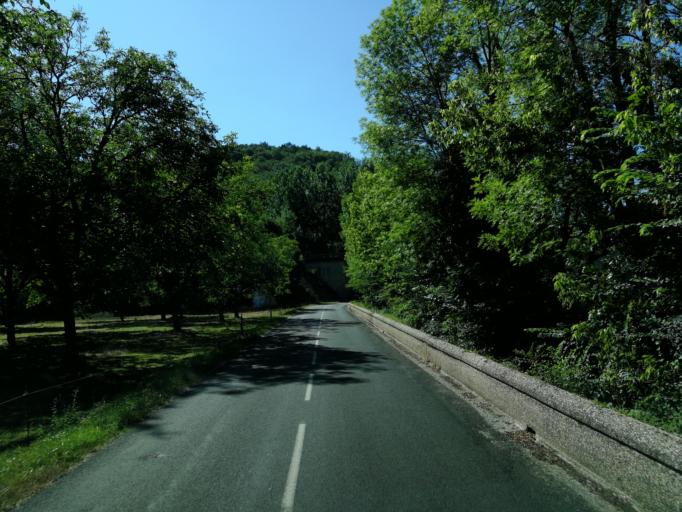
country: FR
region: Midi-Pyrenees
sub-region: Departement du Lot
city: Souillac
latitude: 44.8713
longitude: 1.4133
